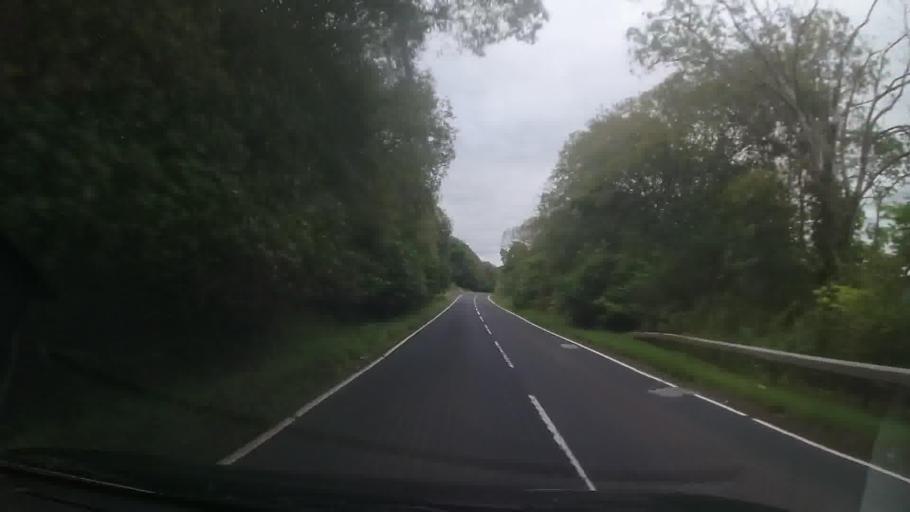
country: GB
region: Scotland
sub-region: Argyll and Bute
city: Garelochhead
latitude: 56.2144
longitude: -5.0465
